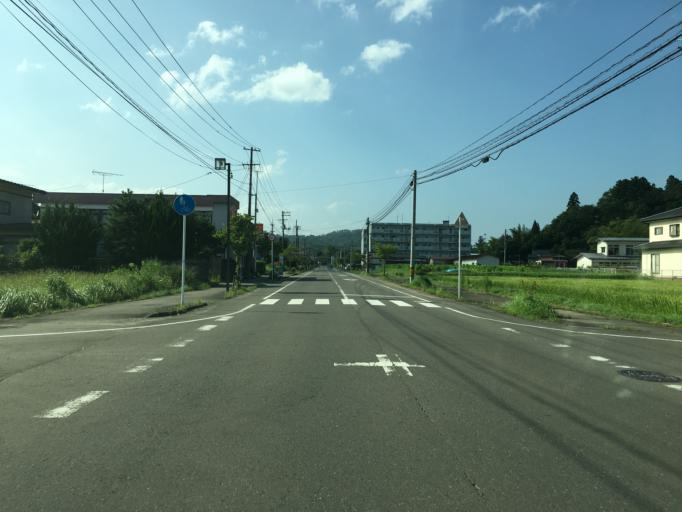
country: JP
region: Miyagi
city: Marumori
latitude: 37.9274
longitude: 140.7641
